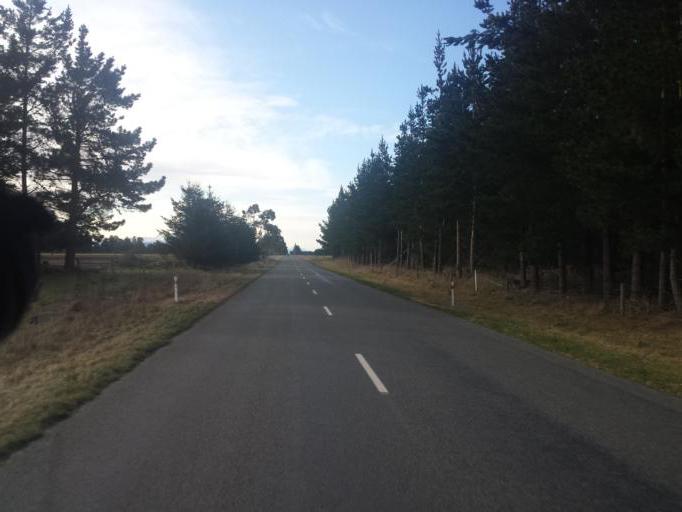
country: NZ
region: Canterbury
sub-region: Ashburton District
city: Tinwald
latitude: -43.9255
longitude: 171.3485
